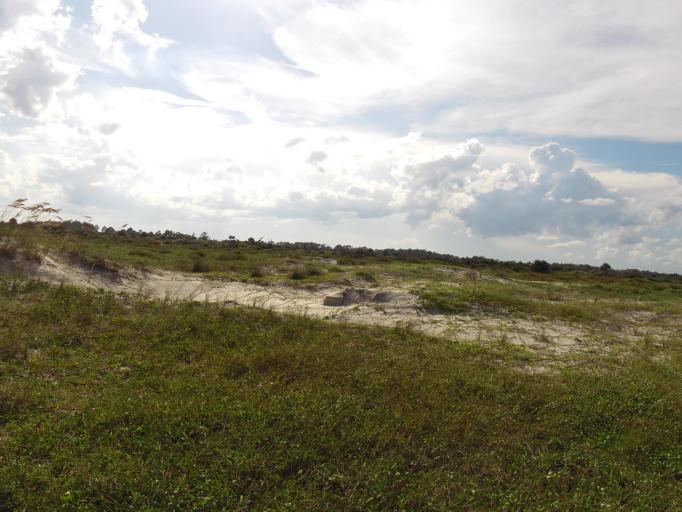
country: US
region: Florida
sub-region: Duval County
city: Atlantic Beach
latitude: 30.4529
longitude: -81.4109
